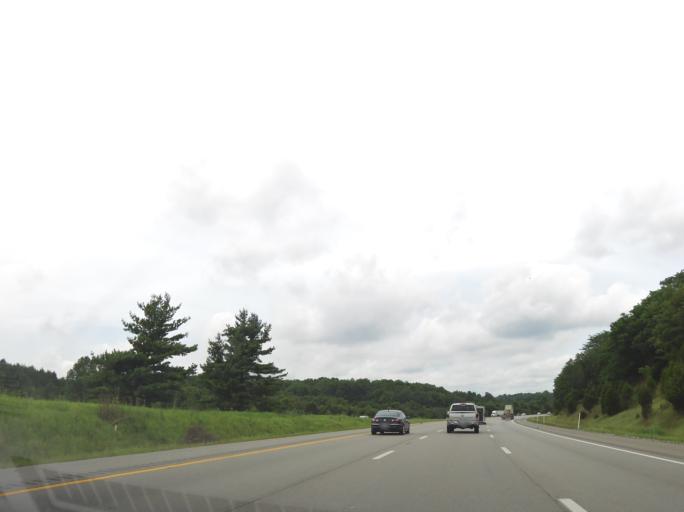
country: US
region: Kentucky
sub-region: Scott County
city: Georgetown
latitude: 38.3412
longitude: -84.5679
